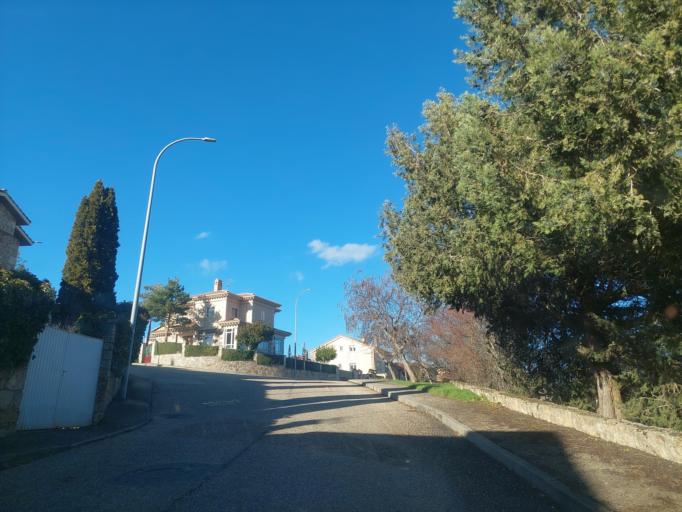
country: ES
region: Castille and Leon
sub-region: Provincia de Segovia
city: Pradena
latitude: 41.1334
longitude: -3.6906
